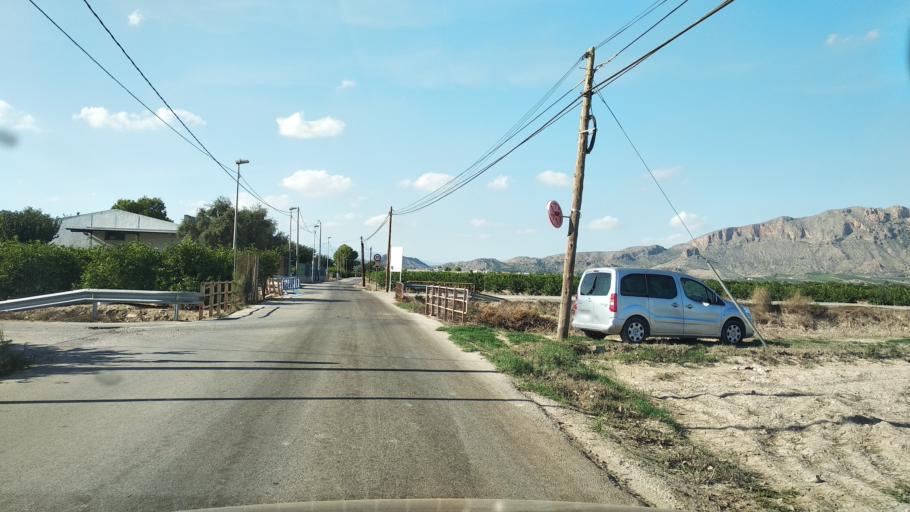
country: ES
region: Murcia
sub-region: Murcia
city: Santomera
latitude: 38.0472
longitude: -1.0383
